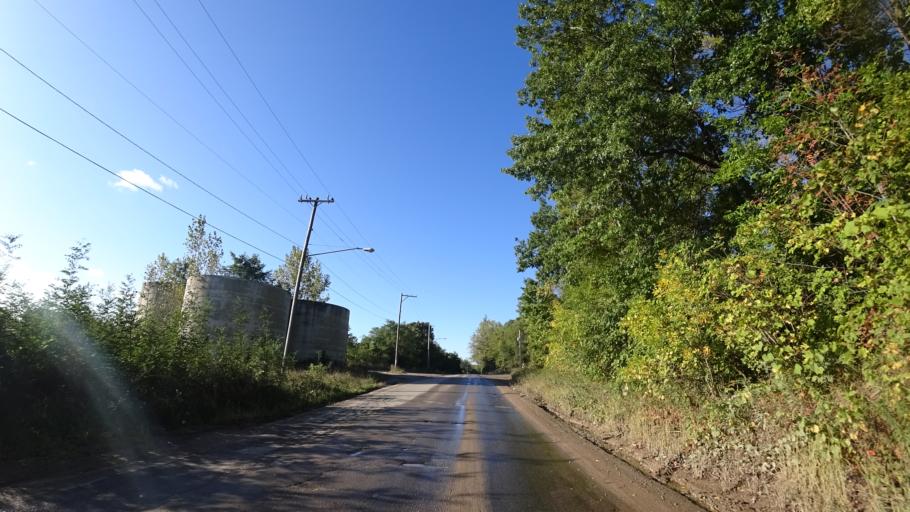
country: US
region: Michigan
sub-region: Kent County
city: Wyoming
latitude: 42.9527
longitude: -85.7092
